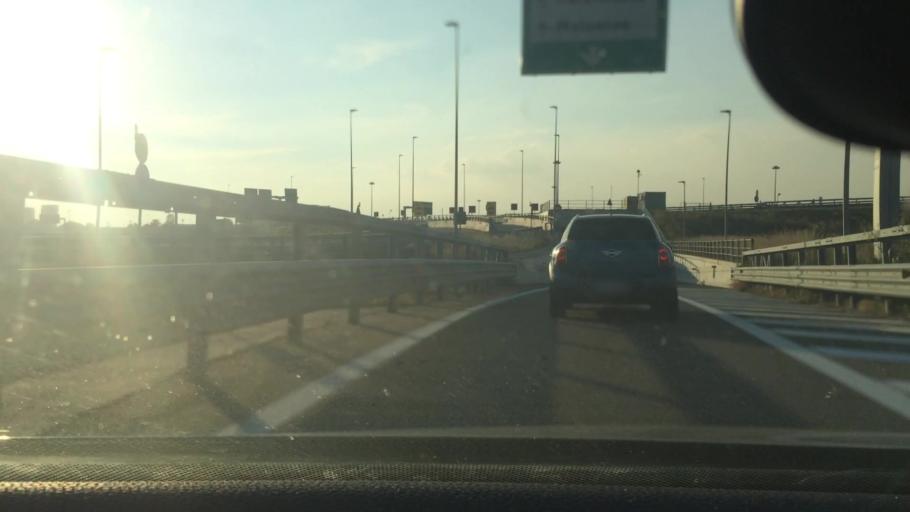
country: IT
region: Lombardy
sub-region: Citta metropolitana di Milano
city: Pero
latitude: 45.5136
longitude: 9.1006
